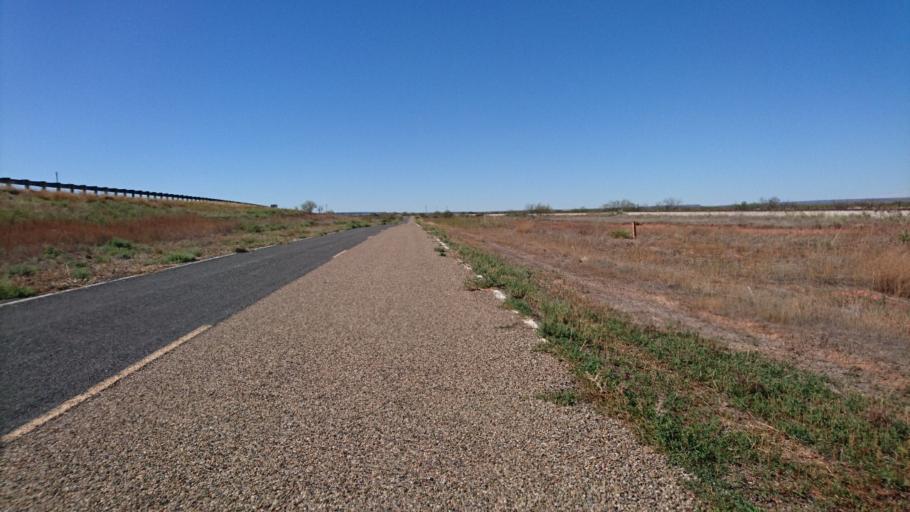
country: US
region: New Mexico
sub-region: Quay County
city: Tucumcari
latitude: 35.1005
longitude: -104.0486
